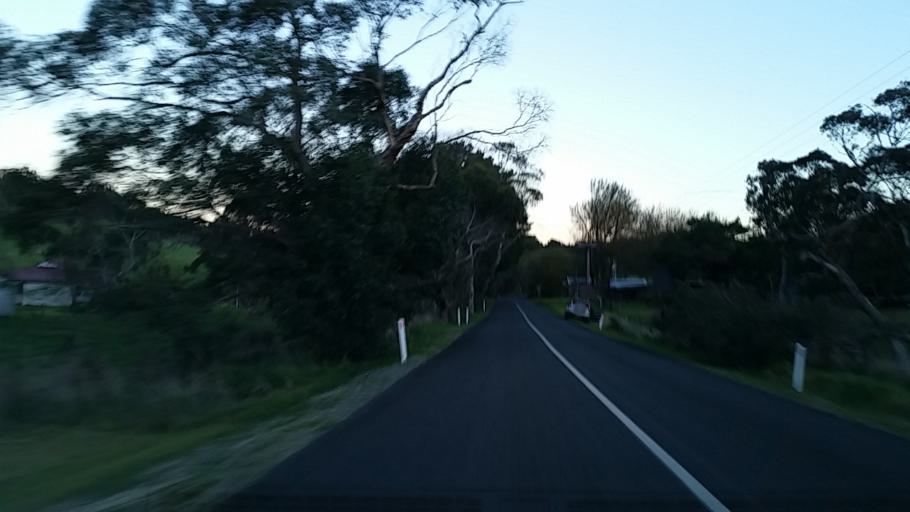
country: AU
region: South Australia
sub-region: Alexandrina
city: Mount Compass
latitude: -35.3037
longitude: 138.6117
